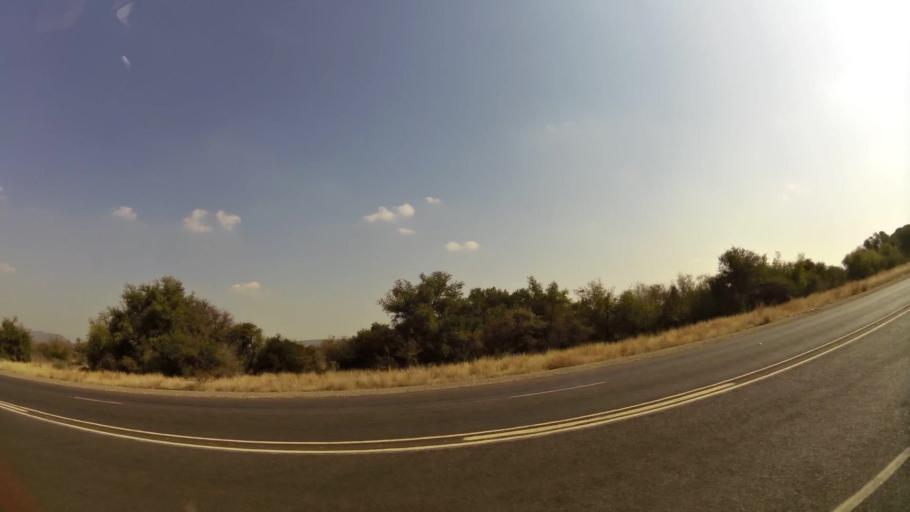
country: ZA
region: North-West
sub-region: Bojanala Platinum District Municipality
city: Mogwase
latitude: -25.4180
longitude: 27.0784
